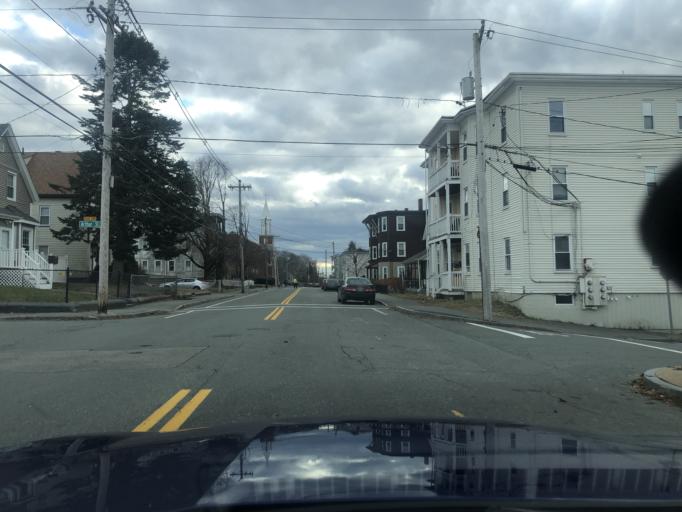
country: US
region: Massachusetts
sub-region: Plymouth County
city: Brockton
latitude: 42.1033
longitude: -71.0131
